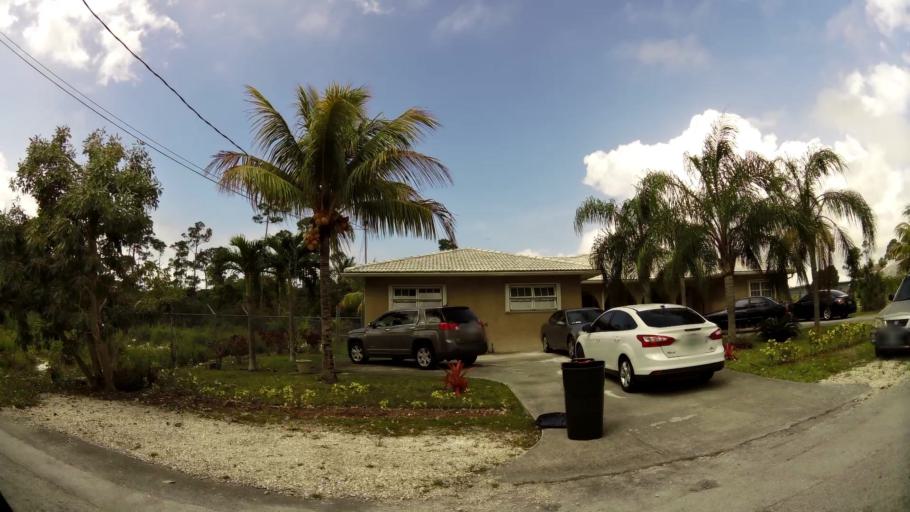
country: BS
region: Freeport
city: Lucaya
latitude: 26.5454
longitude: -78.5855
